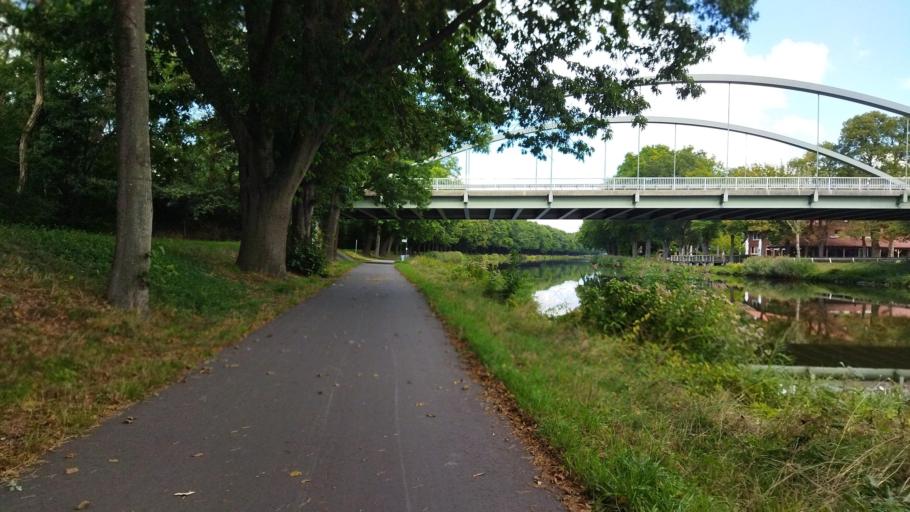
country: DE
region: Lower Saxony
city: Lingen
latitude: 52.4942
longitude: 7.2953
